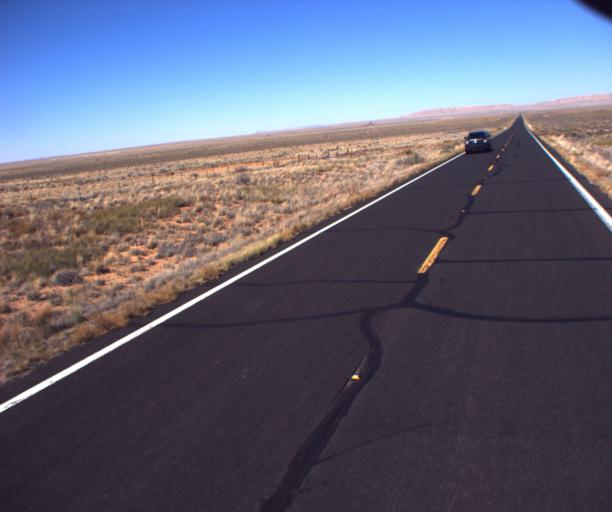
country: US
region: Arizona
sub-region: Navajo County
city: First Mesa
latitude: 35.6742
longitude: -110.4979
